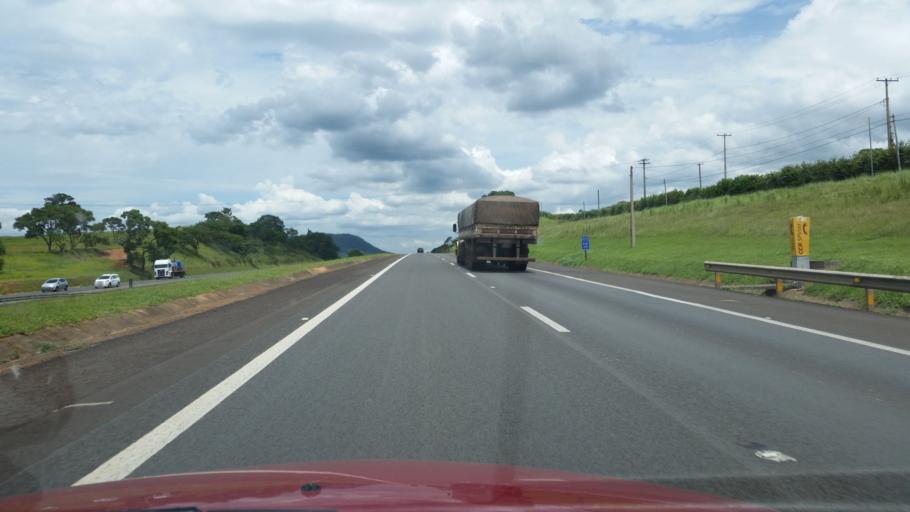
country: BR
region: Sao Paulo
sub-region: Itatinga
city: Itatinga
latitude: -23.1436
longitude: -48.4167
